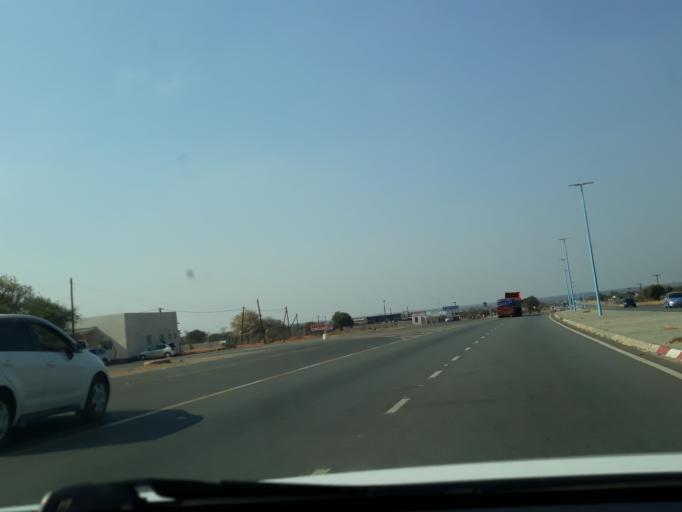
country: BW
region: Central
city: Tonota
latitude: -21.4218
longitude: 27.4430
